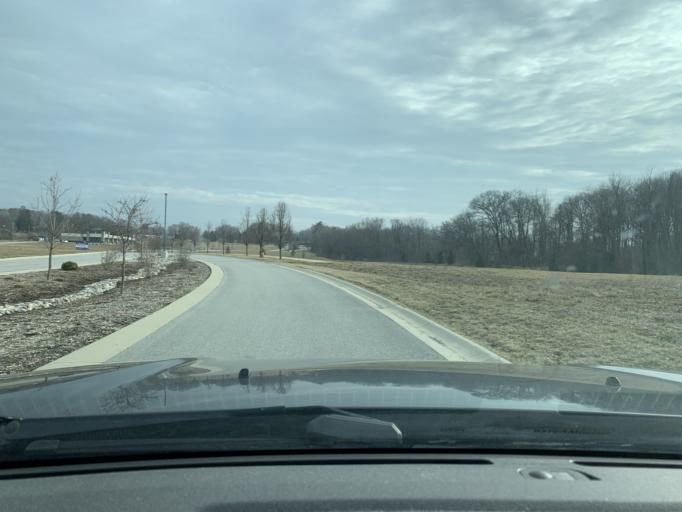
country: US
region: Indiana
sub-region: Porter County
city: Chesterton
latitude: 41.5547
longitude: -87.0547
